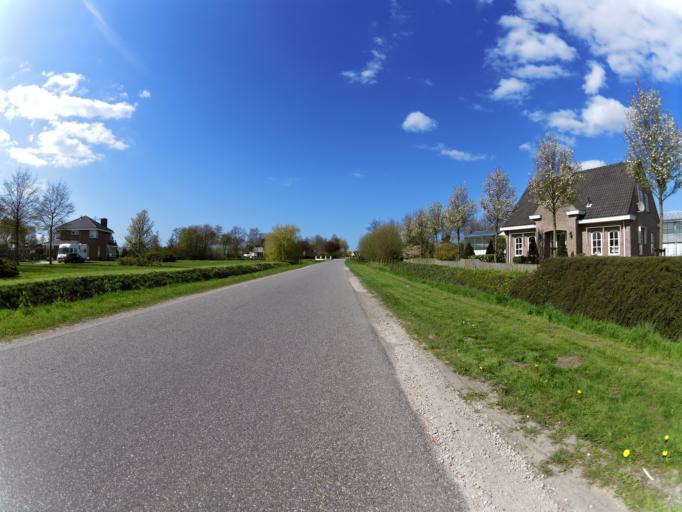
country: NL
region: South Holland
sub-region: Gemeente Brielle
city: Brielle
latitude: 51.9047
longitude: 4.1423
